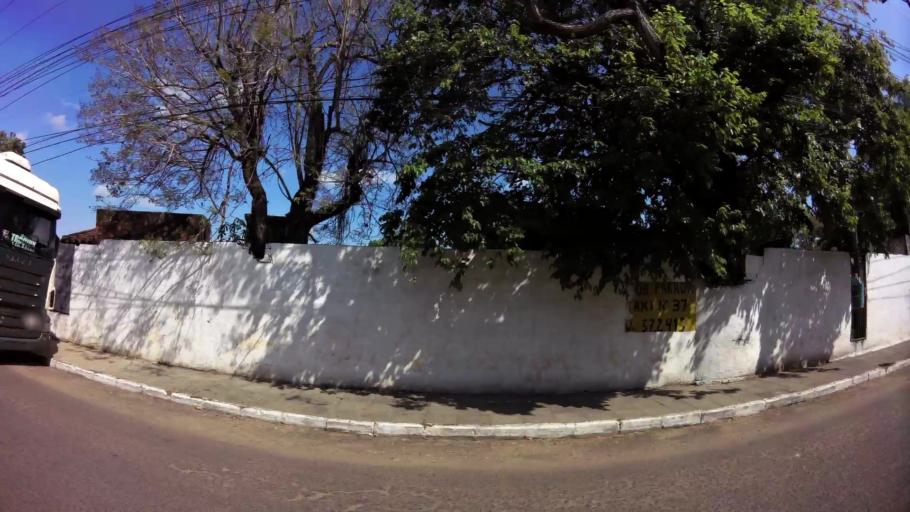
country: PY
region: Central
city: San Lorenzo
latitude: -25.3453
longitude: -57.5017
